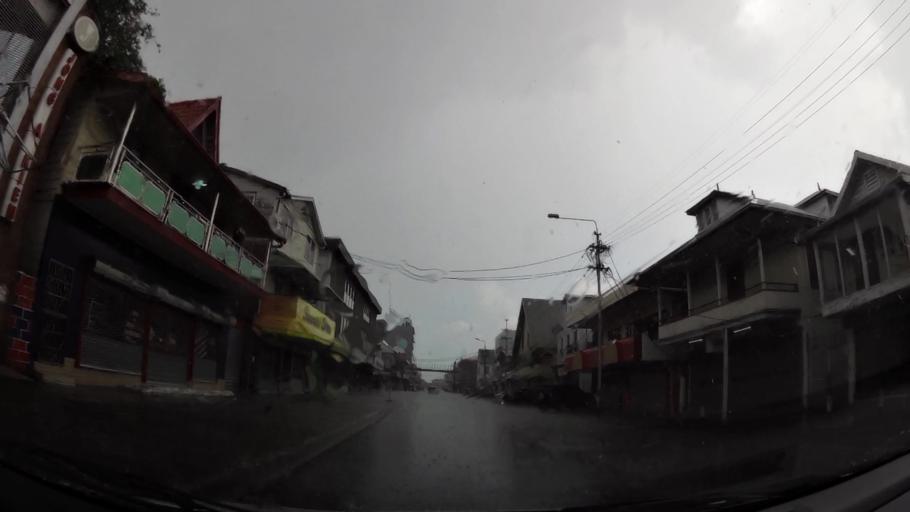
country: SR
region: Paramaribo
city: Paramaribo
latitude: 5.8274
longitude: -55.1611
